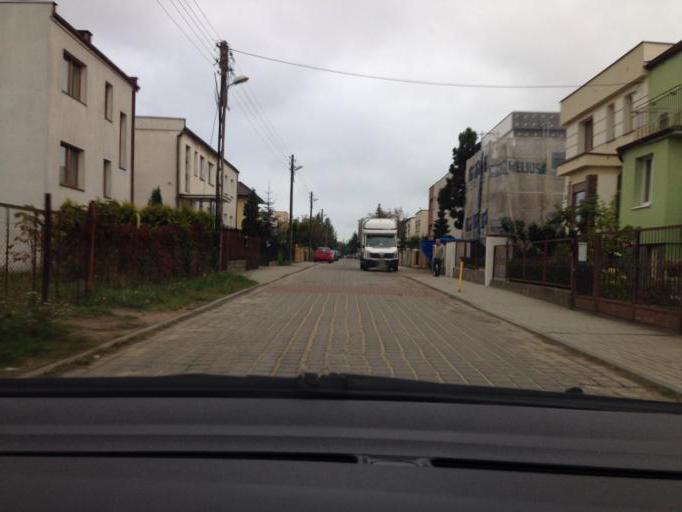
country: PL
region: Greater Poland Voivodeship
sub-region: Powiat poznanski
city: Suchy Las
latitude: 52.4591
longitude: 16.8781
